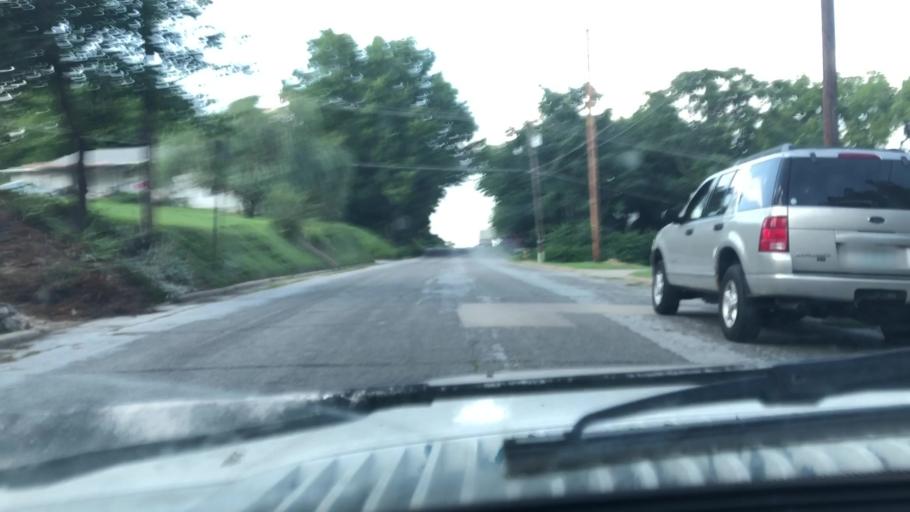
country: US
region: Missouri
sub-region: Newton County
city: Neosho
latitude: 36.8639
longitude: -94.3663
